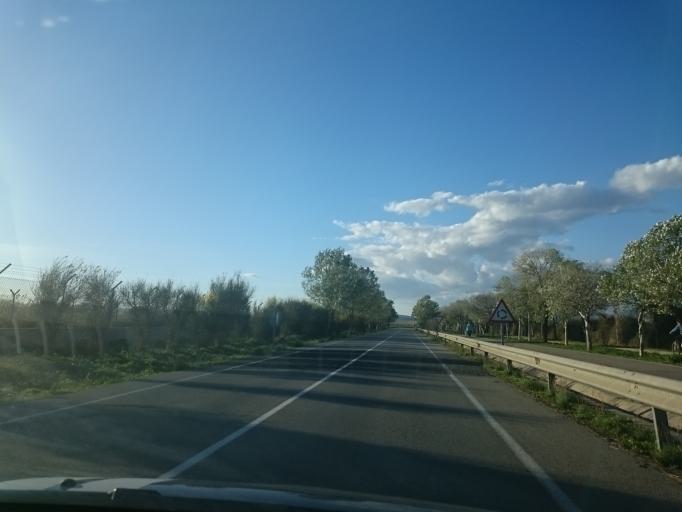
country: ES
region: Catalonia
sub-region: Provincia de Barcelona
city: El Prat de Llobregat
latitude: 41.2961
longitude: 2.1021
